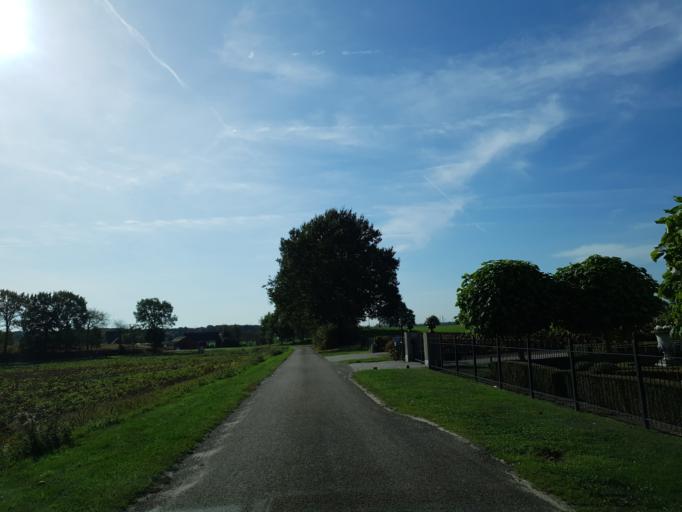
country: NL
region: North Brabant
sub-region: Gemeente Woensdrecht
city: Woensdrecht
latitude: 51.3849
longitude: 4.3334
